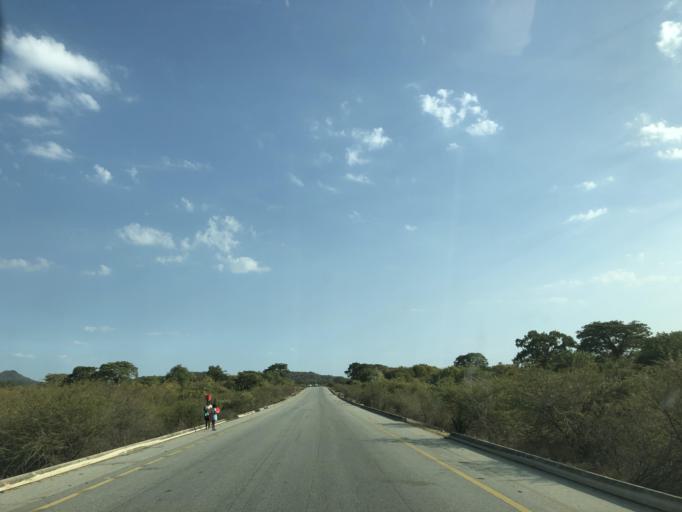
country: AO
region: Benguela
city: Benguela
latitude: -13.2376
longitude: 13.7713
